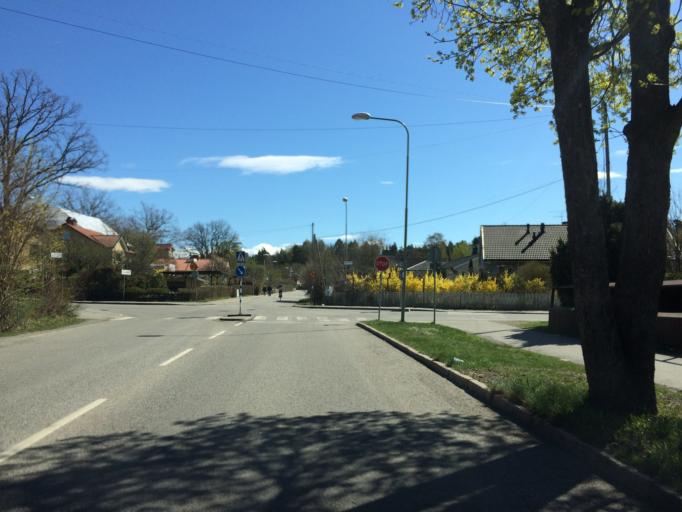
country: SE
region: Stockholm
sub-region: Huddinge Kommun
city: Huddinge
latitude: 59.2740
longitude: 17.9877
